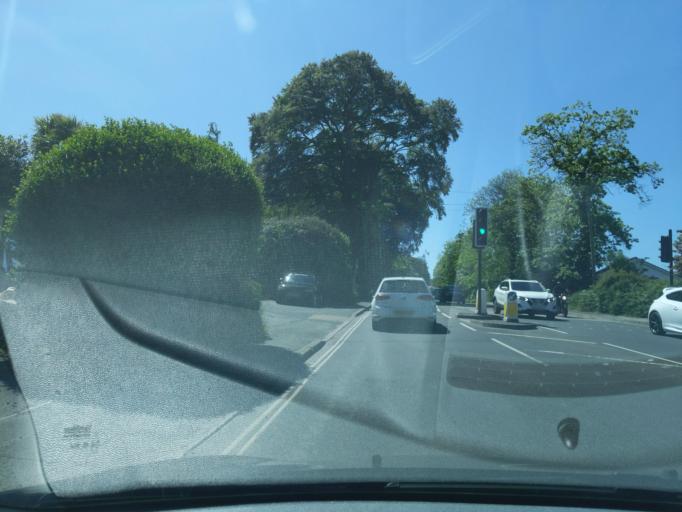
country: GB
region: England
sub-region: Cornwall
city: St Austell
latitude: 50.3387
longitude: -4.7617
